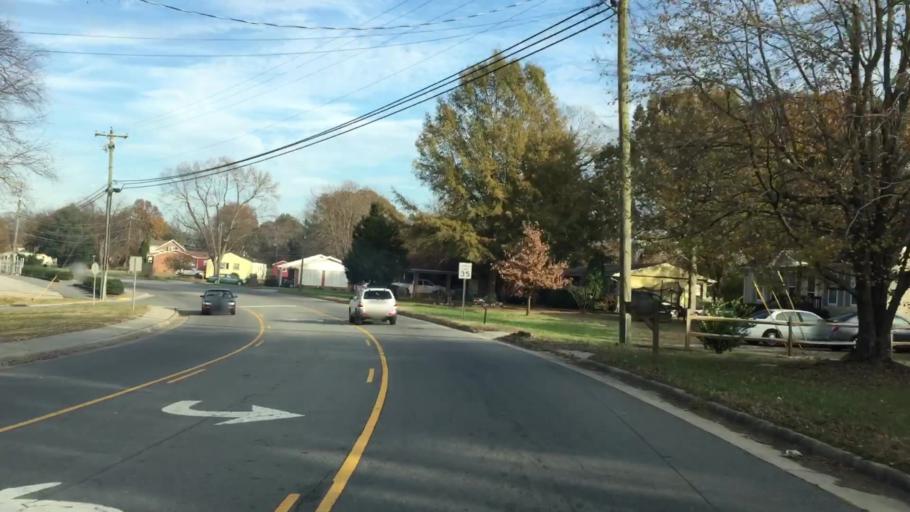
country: US
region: North Carolina
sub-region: Rockingham County
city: Reidsville
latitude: 36.3523
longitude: -79.6829
